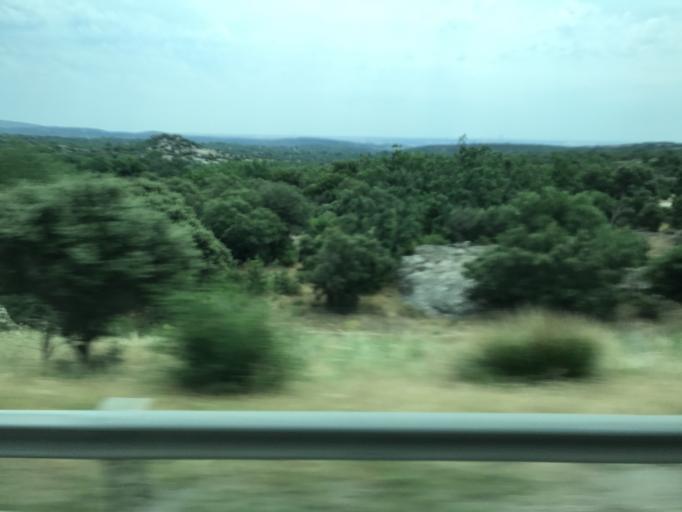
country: ES
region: Madrid
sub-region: Provincia de Madrid
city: La Cabrera
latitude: 40.8584
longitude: -3.6095
